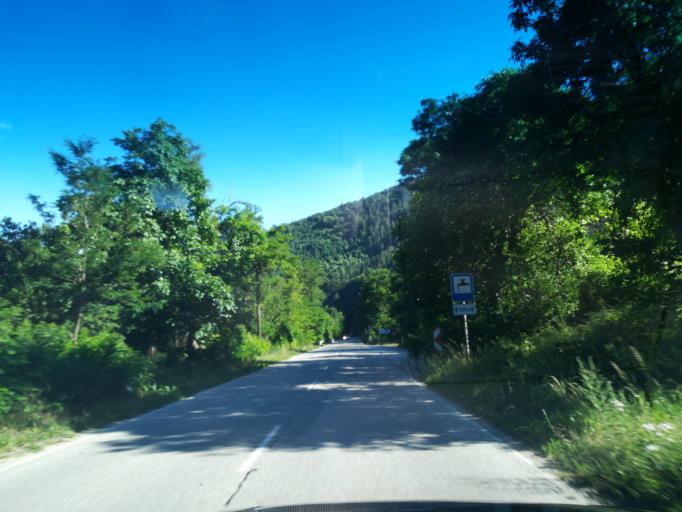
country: BG
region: Smolyan
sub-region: Obshtina Chepelare
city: Chepelare
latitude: 41.8399
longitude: 24.6795
